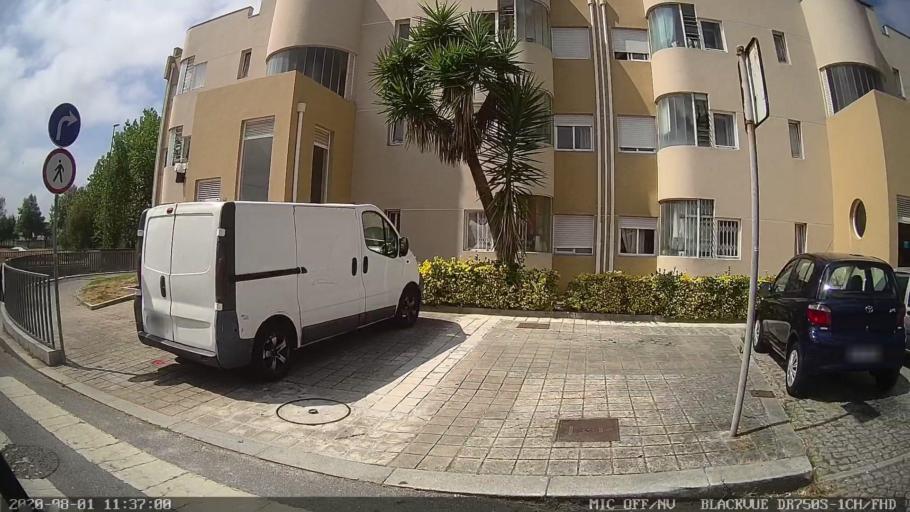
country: PT
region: Porto
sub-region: Matosinhos
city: Senhora da Hora
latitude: 41.1757
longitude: -8.6439
